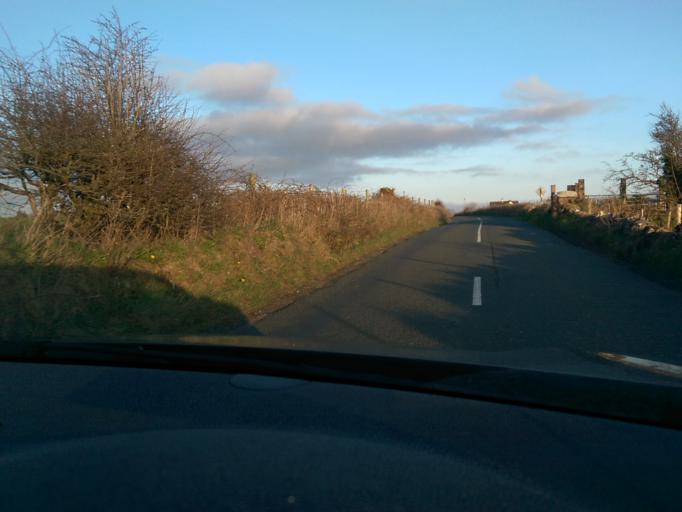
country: IE
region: Connaught
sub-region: Sligo
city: Tobercurry
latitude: 54.0495
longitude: -8.6967
